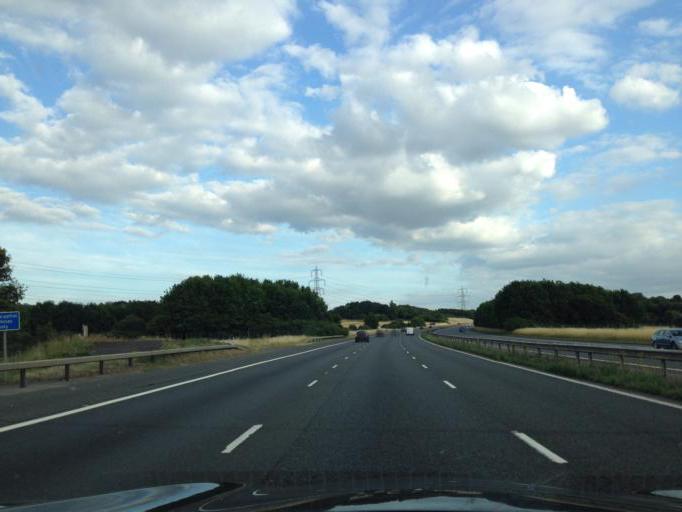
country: GB
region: England
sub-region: Oxfordshire
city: Bicester
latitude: 51.8283
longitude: -1.1137
